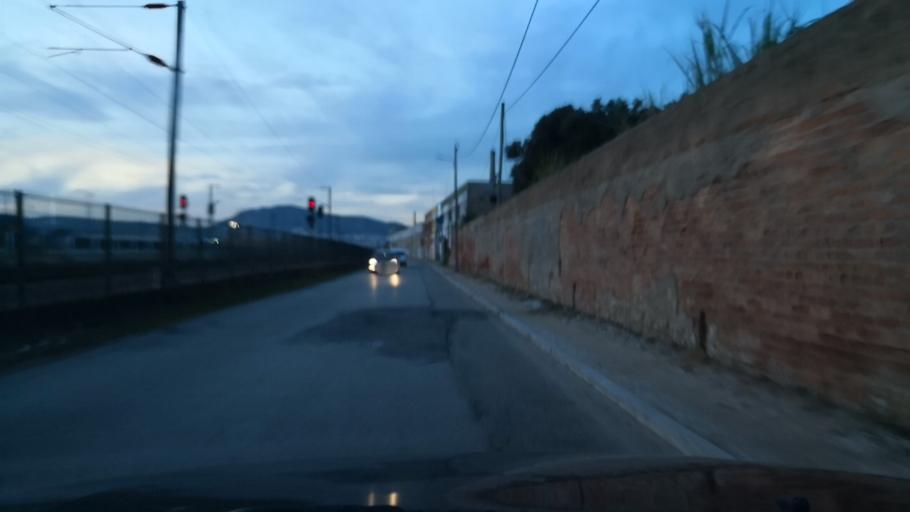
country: PT
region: Setubal
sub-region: Setubal
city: Setubal
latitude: 38.5165
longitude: -8.8691
